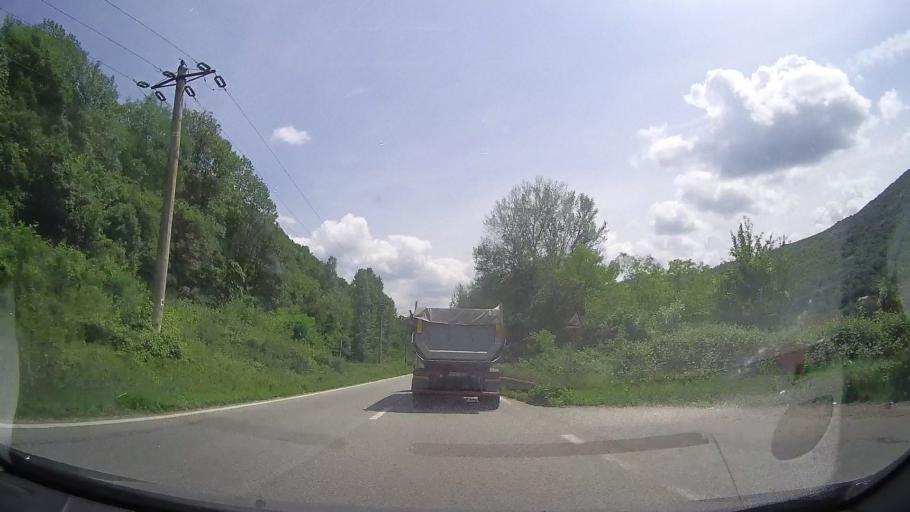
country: RO
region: Valcea
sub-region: Oras Calimanesti
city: Calimanesti
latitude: 45.2763
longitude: 24.3149
